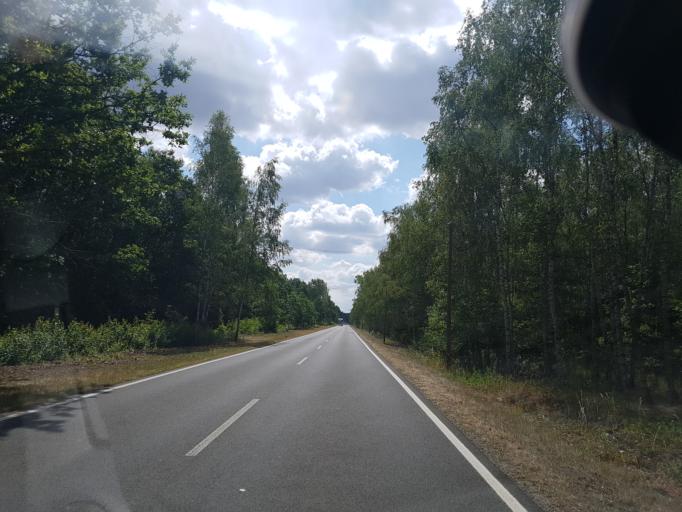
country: DE
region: Brandenburg
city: Drebkau
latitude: 51.6760
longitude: 14.1646
